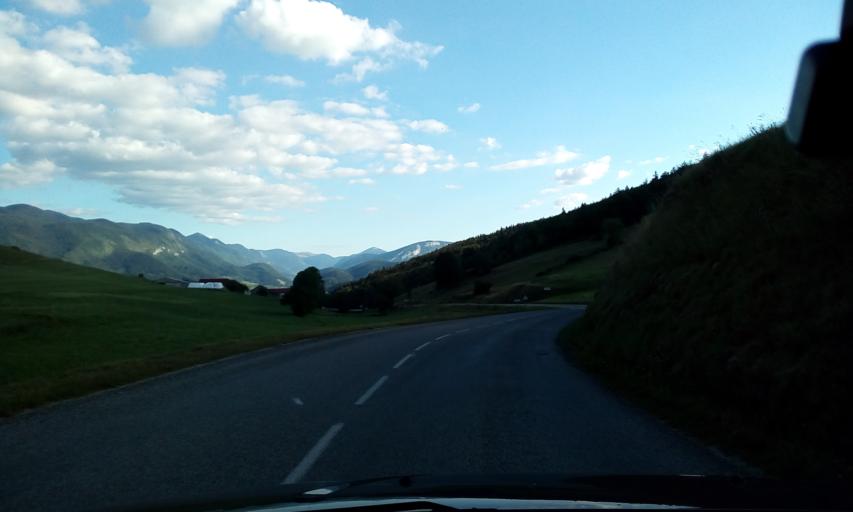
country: FR
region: Rhone-Alpes
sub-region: Departement de l'Isere
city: Pont-en-Royans
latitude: 45.0400
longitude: 5.4455
